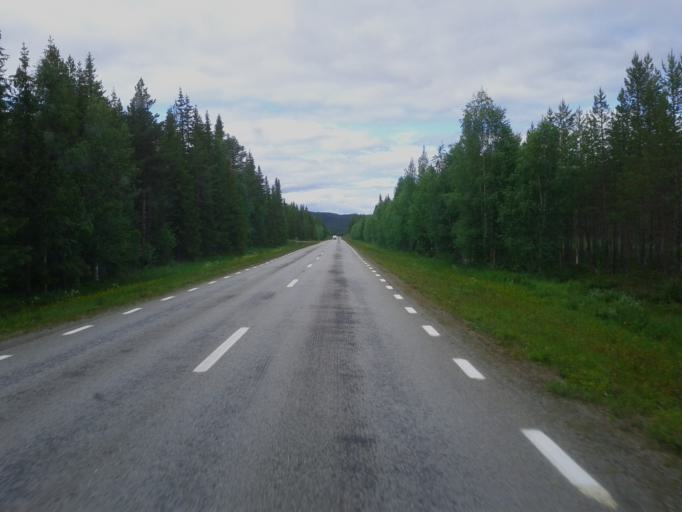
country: SE
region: Vaesterbotten
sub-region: Storumans Kommun
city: Fristad
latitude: 65.3559
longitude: 16.5614
